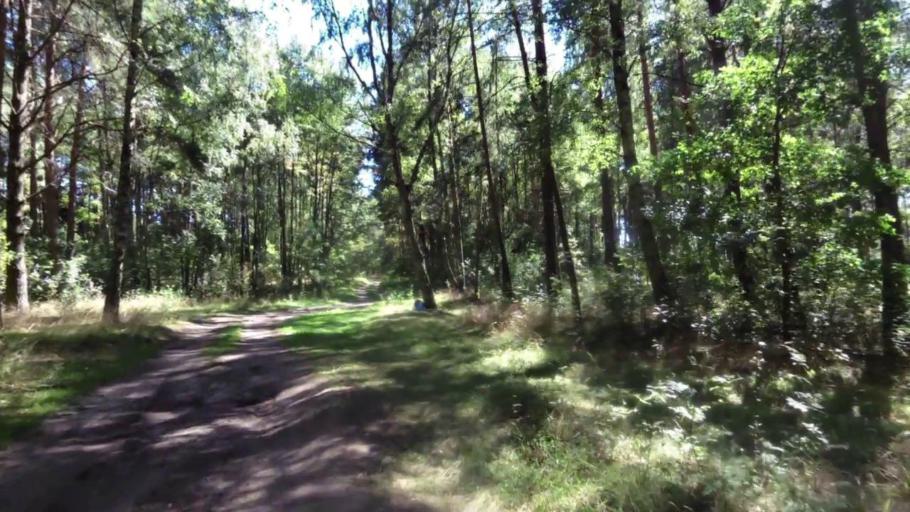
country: PL
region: West Pomeranian Voivodeship
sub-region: Powiat szczecinecki
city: Bialy Bor
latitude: 53.8481
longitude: 16.8711
